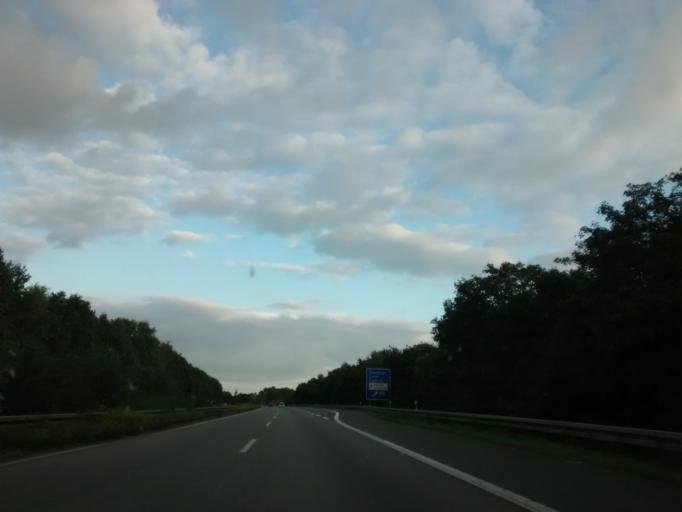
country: DE
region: North Rhine-Westphalia
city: Ibbenburen
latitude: 52.2589
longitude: 7.7025
